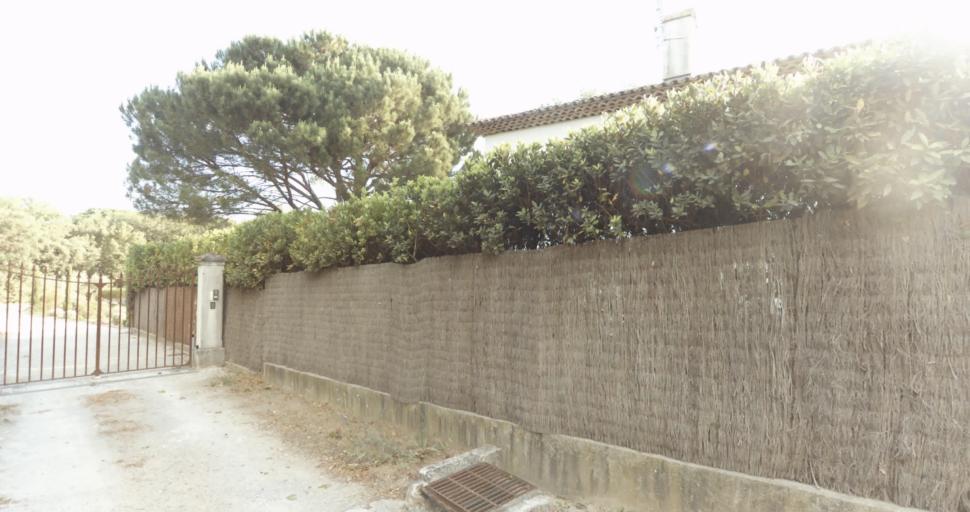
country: FR
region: Provence-Alpes-Cote d'Azur
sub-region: Departement du Var
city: Saint-Tropez
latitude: 43.2583
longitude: 6.6266
